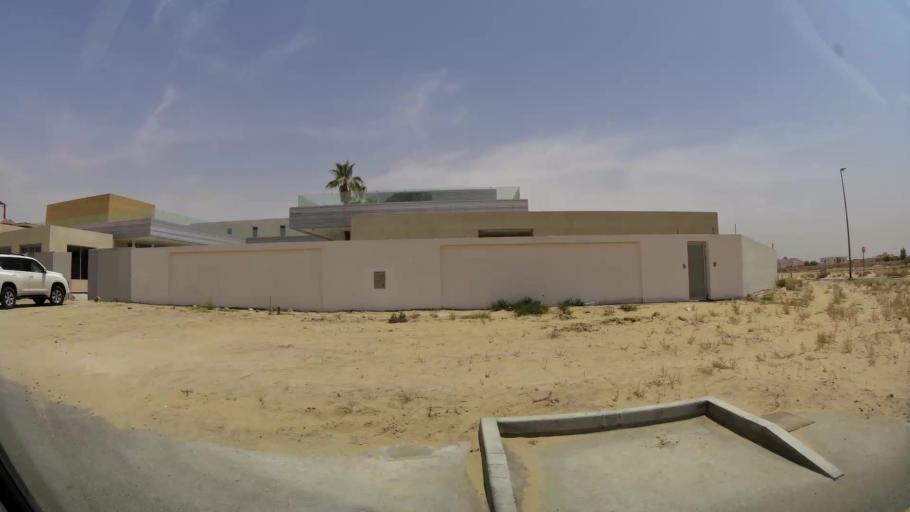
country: AE
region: Ash Shariqah
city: Sharjah
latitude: 25.2481
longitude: 55.4774
